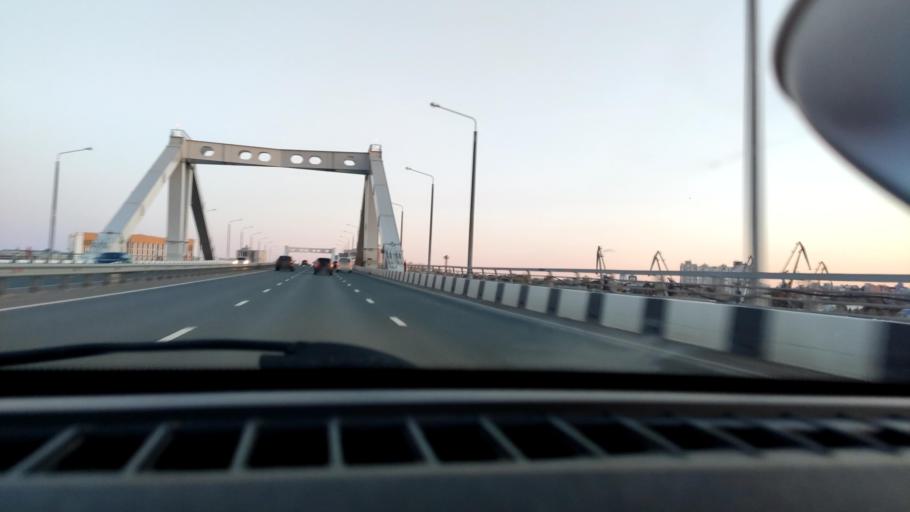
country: RU
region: Samara
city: Samara
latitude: 53.1727
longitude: 50.0861
